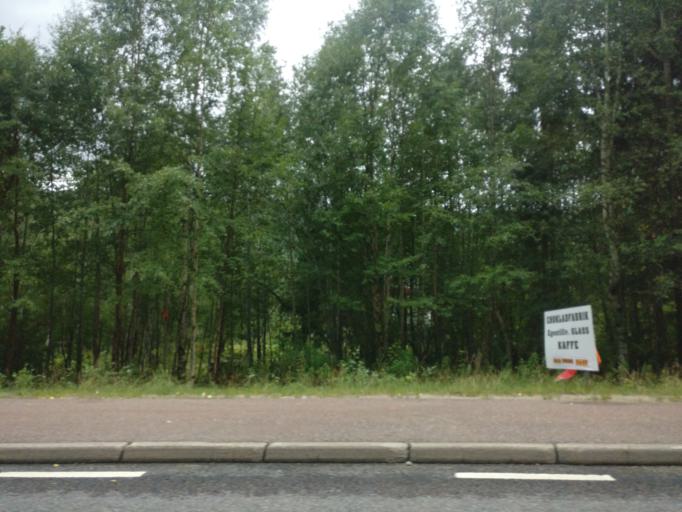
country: SE
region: Vaermland
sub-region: Torsby Kommun
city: Torsby
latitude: 60.7151
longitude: 12.8809
